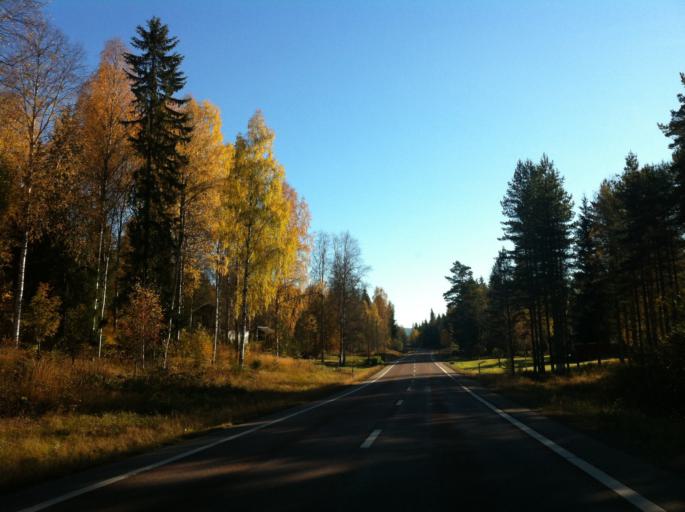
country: SE
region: Dalarna
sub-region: Alvdalens Kommun
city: AElvdalen
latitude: 61.1773
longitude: 14.0993
